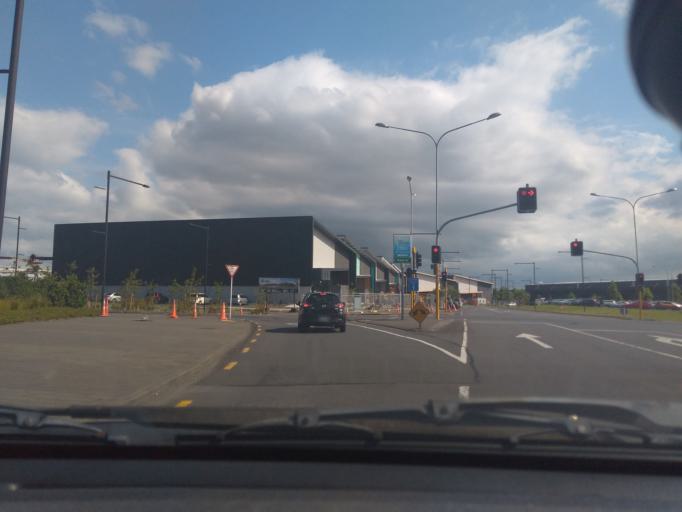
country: NZ
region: Auckland
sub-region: Auckland
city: Tamaki
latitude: -36.9380
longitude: 174.8756
